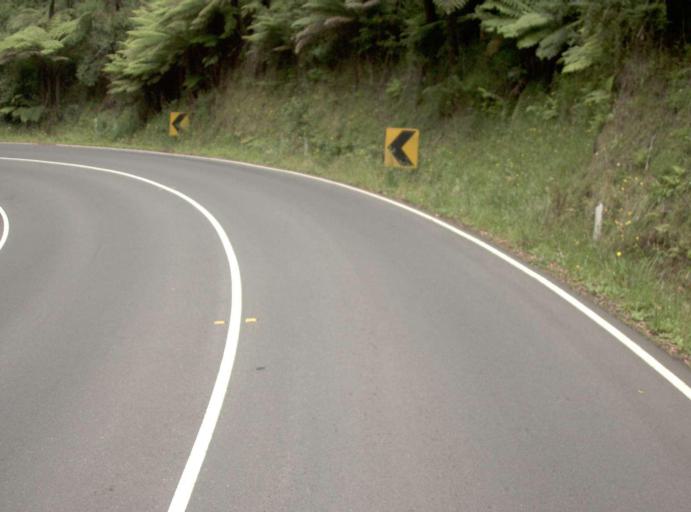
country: AU
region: Victoria
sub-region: Yarra Ranges
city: Healesville
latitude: -37.5934
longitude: 145.6390
